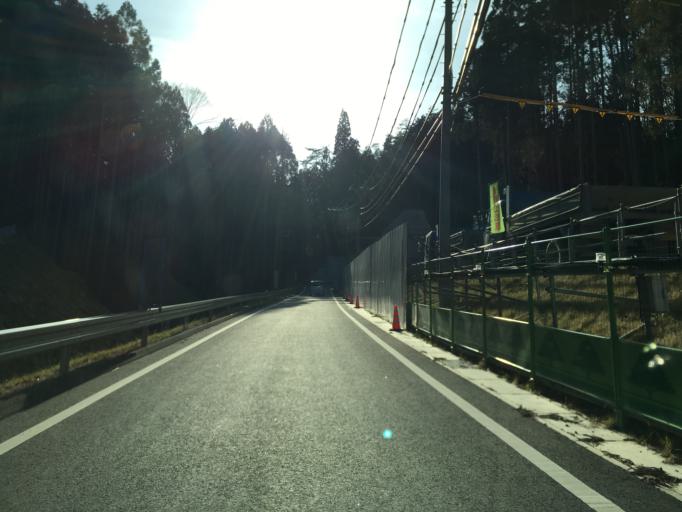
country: JP
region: Ibaraki
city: Daigo
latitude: 36.7110
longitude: 140.4897
